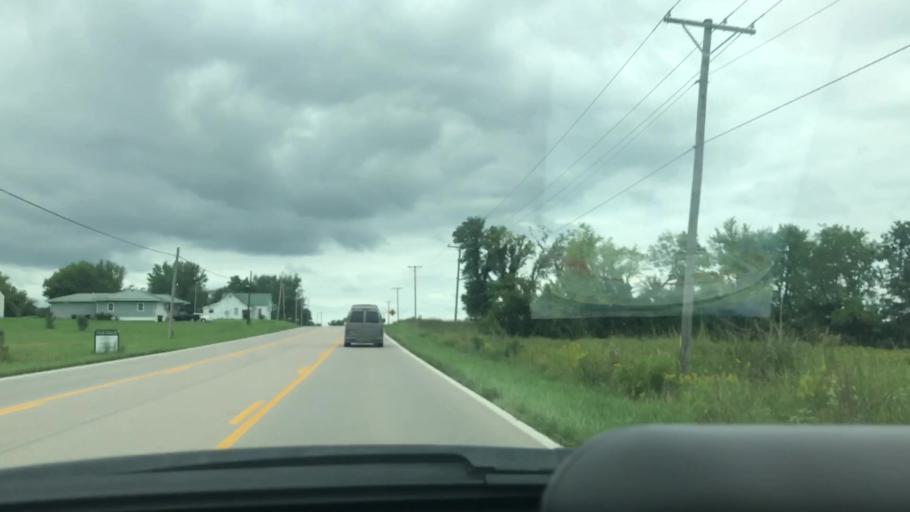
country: US
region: Missouri
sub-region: Dallas County
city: Buffalo
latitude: 37.6502
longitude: -93.1039
